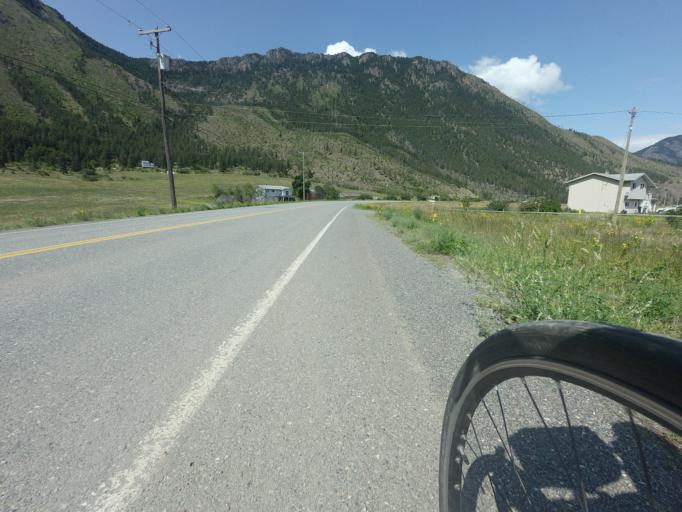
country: CA
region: British Columbia
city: Lillooet
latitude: 50.7420
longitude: -121.8818
